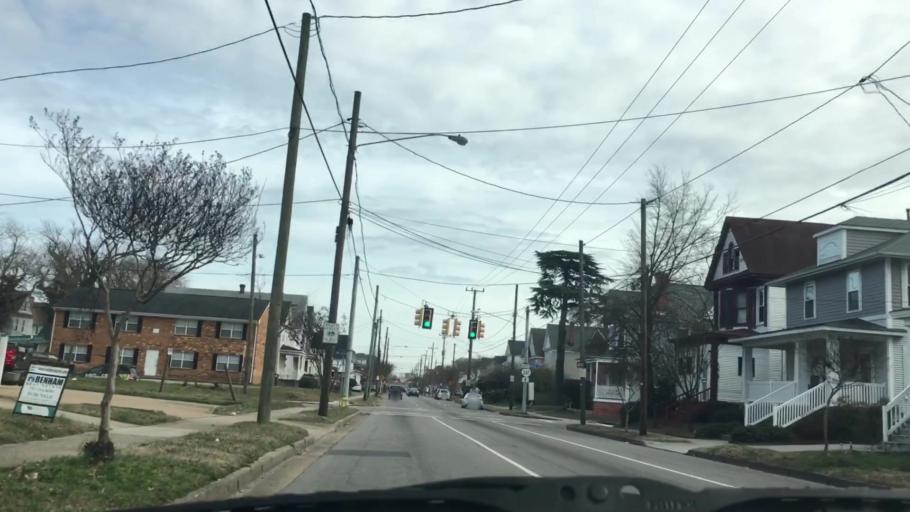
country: US
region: Virginia
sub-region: City of Norfolk
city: Norfolk
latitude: 36.8722
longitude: -76.2875
